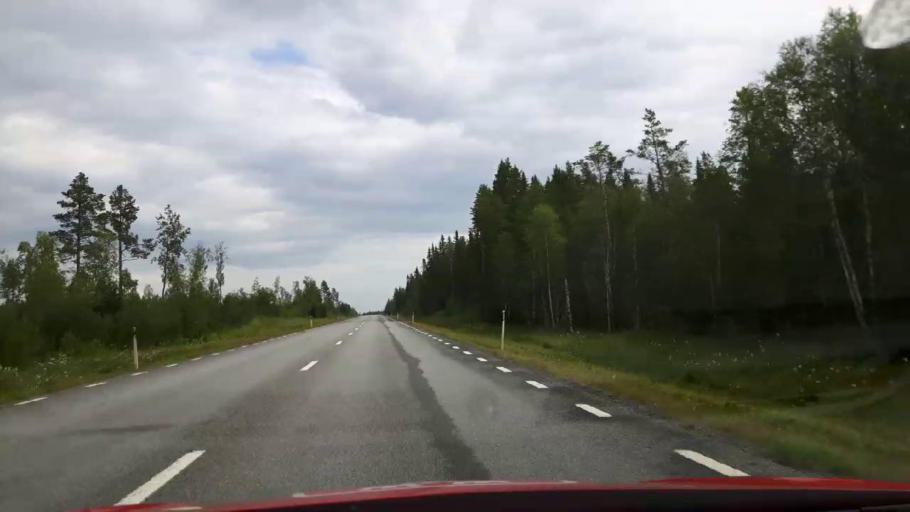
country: SE
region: Jaemtland
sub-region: Stroemsunds Kommun
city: Stroemsund
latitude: 63.6984
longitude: 15.4356
